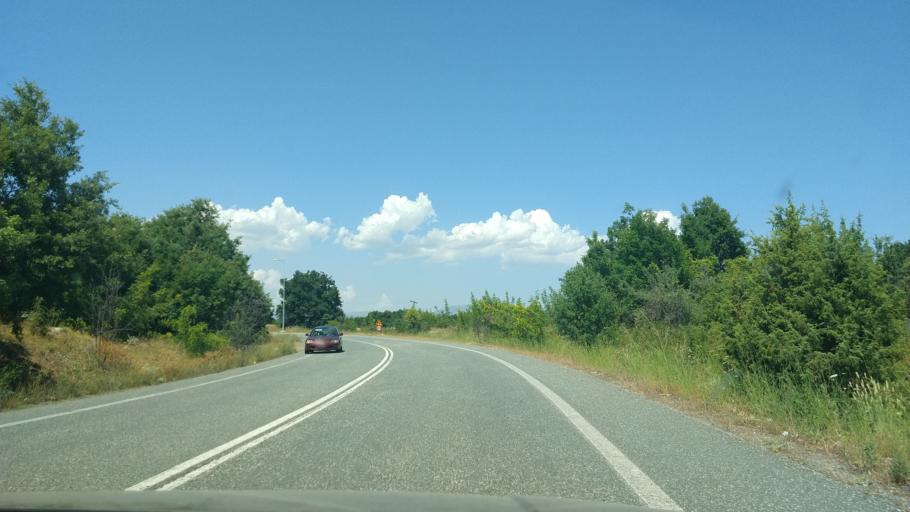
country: GR
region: West Macedonia
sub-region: Nomos Grevenon
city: Grevena
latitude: 40.0638
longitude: 21.4689
